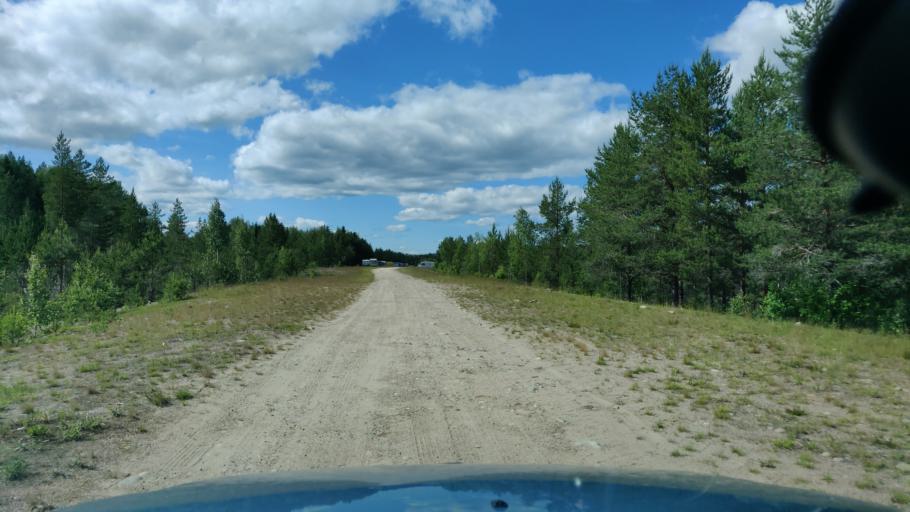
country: NO
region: Hedmark
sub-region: Trysil
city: Innbygda
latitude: 60.9066
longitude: 12.5714
